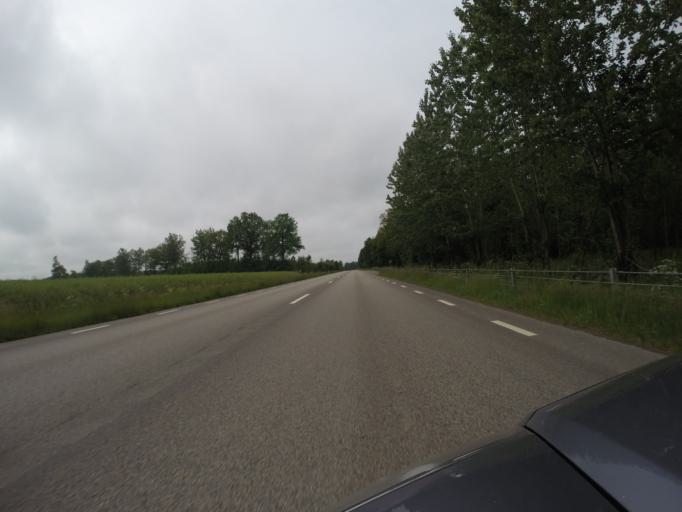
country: SE
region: Skane
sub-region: Bjuvs Kommun
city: Billesholm
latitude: 56.0228
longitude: 12.9632
